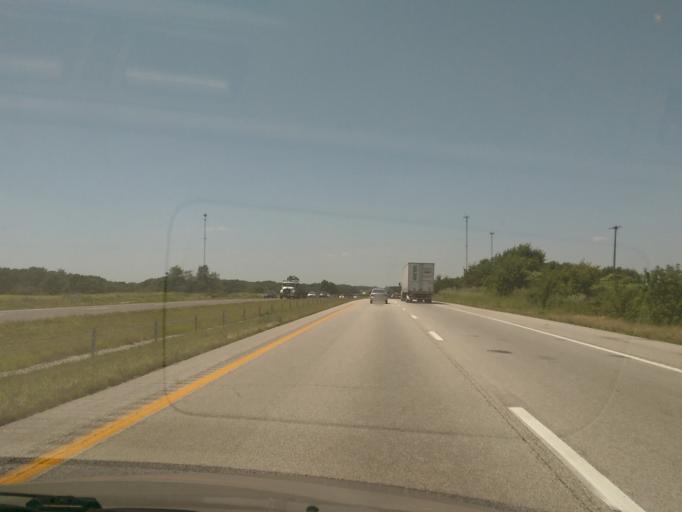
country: US
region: Missouri
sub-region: Saline County
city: Marshall
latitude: 38.9492
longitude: -93.0282
